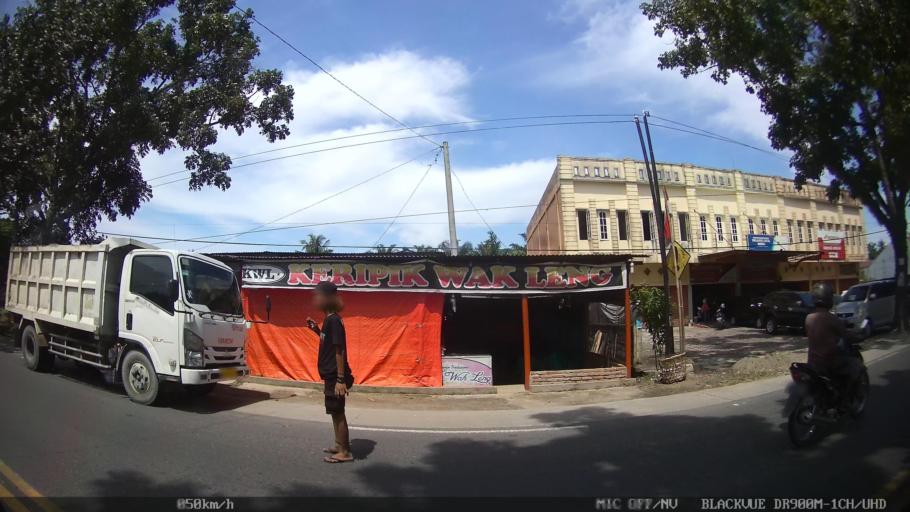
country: ID
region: North Sumatra
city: Binjai
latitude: 3.6407
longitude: 98.5102
